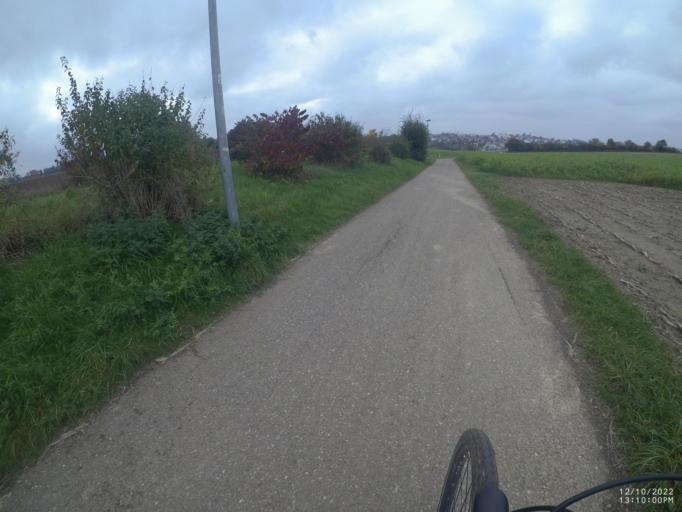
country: DE
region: Baden-Wuerttemberg
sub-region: Regierungsbezirk Stuttgart
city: Ebersbach an der Fils
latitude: 48.7079
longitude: 9.5359
